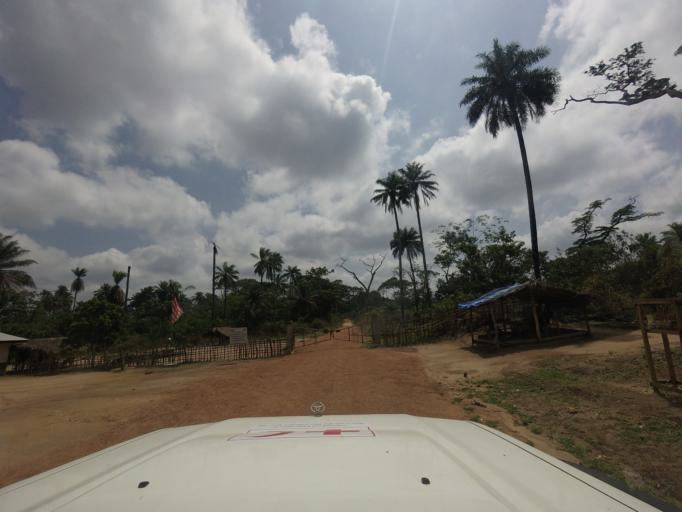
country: LR
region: Lofa
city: Voinjama
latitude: 8.4605
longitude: -9.6347
